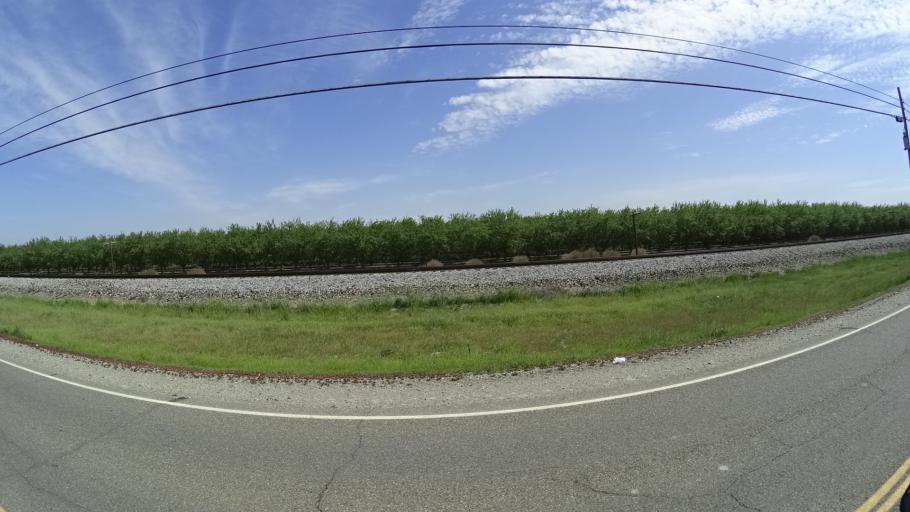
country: US
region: California
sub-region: Glenn County
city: Willows
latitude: 39.5777
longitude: -122.1938
